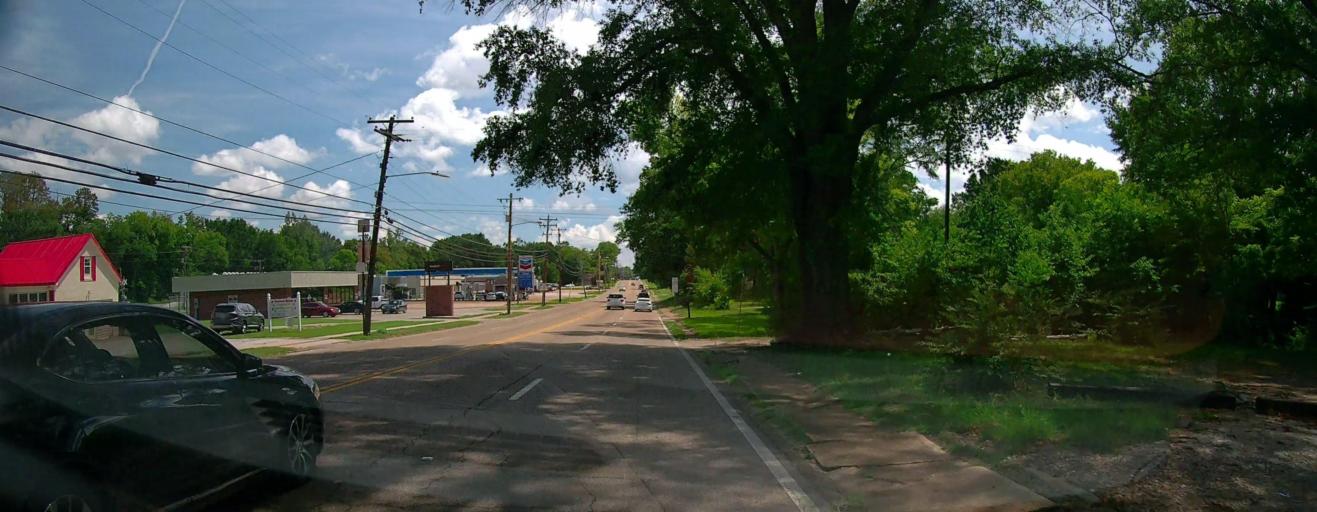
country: US
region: Mississippi
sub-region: Lee County
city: Verona
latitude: 34.2002
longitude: -88.7201
